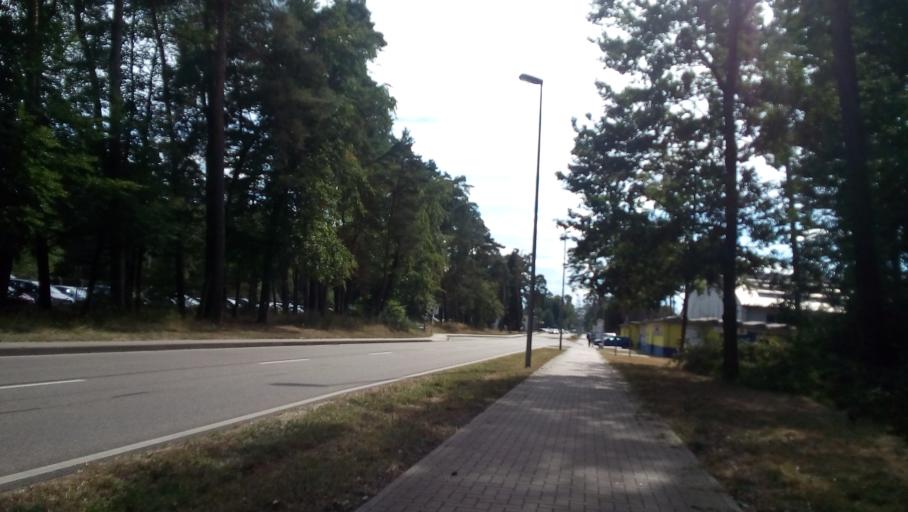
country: DE
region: Baden-Wuerttemberg
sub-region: Karlsruhe Region
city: Hugelsheim
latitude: 48.7828
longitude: 8.0984
